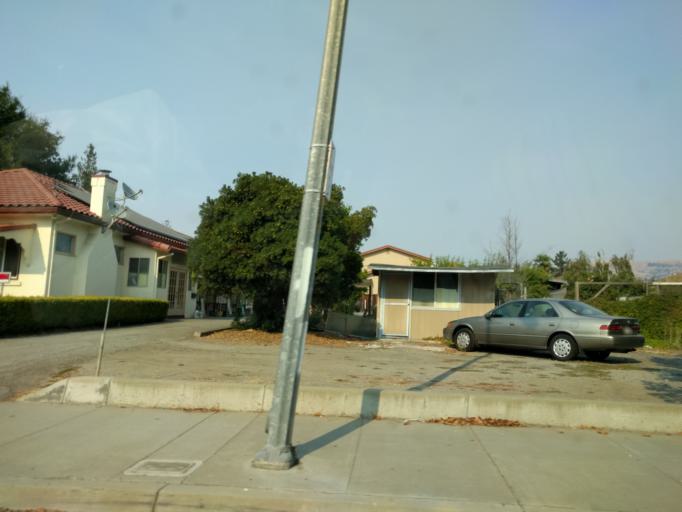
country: US
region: California
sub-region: Santa Clara County
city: Alum Rock
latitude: 37.3771
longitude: -121.8499
